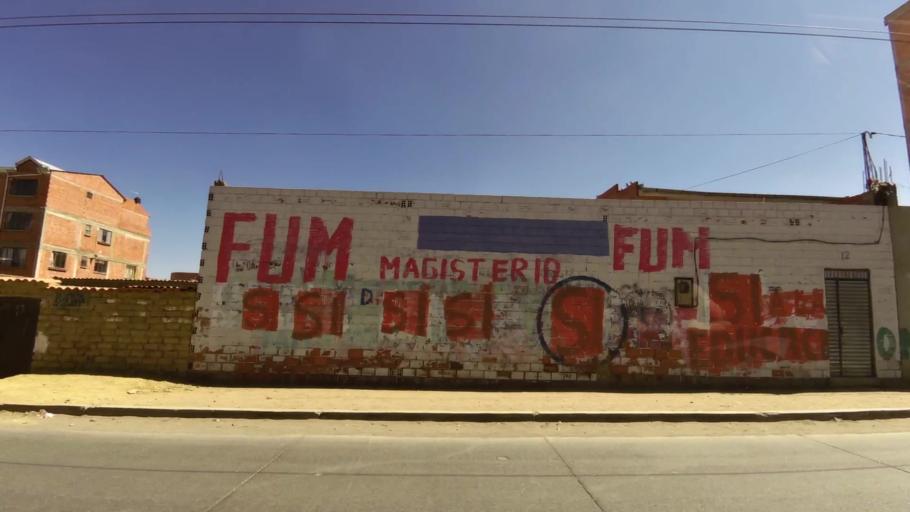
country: BO
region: La Paz
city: La Paz
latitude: -16.4948
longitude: -68.2051
